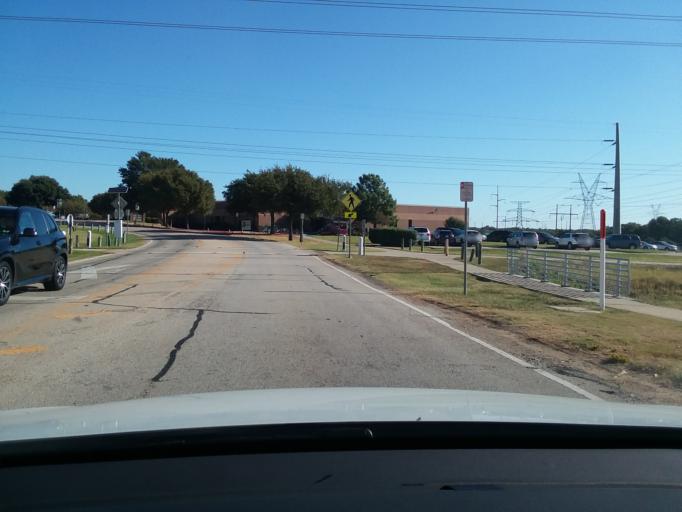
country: US
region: Texas
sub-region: Denton County
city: Highland Village
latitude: 33.0796
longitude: -97.0668
